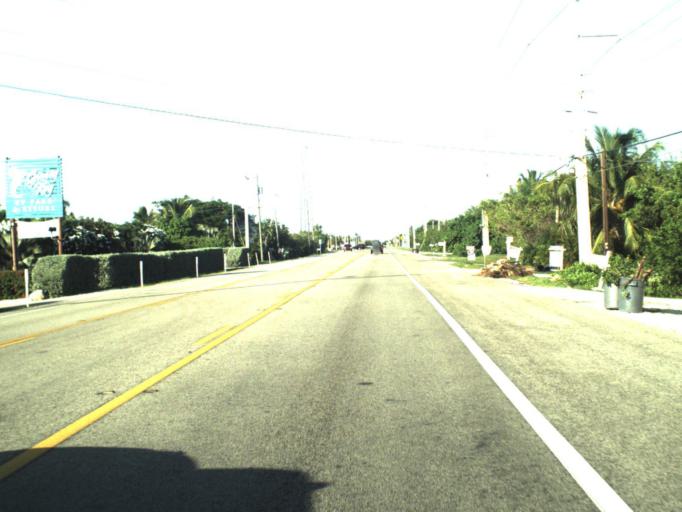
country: US
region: Florida
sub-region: Monroe County
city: Marathon
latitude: 24.7641
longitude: -80.9486
